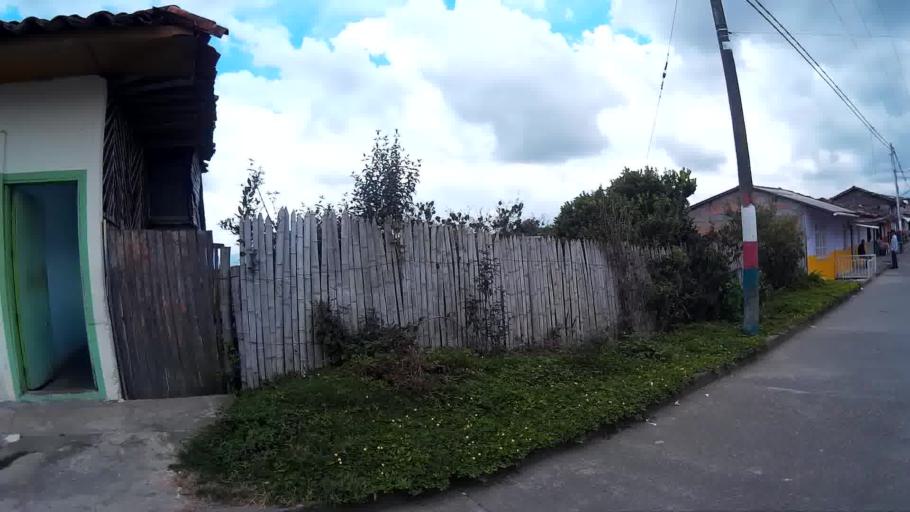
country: CO
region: Valle del Cauca
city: Ulloa
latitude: 4.7190
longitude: -75.7165
